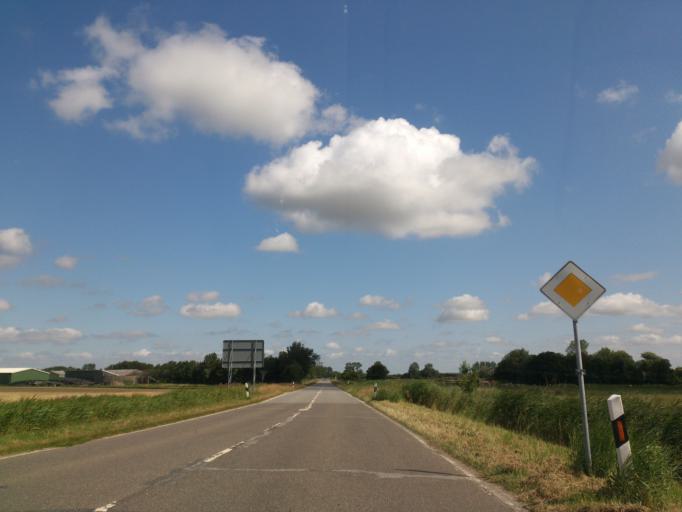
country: DE
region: Schleswig-Holstein
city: Vollerwiek
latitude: 54.2945
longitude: 8.8246
